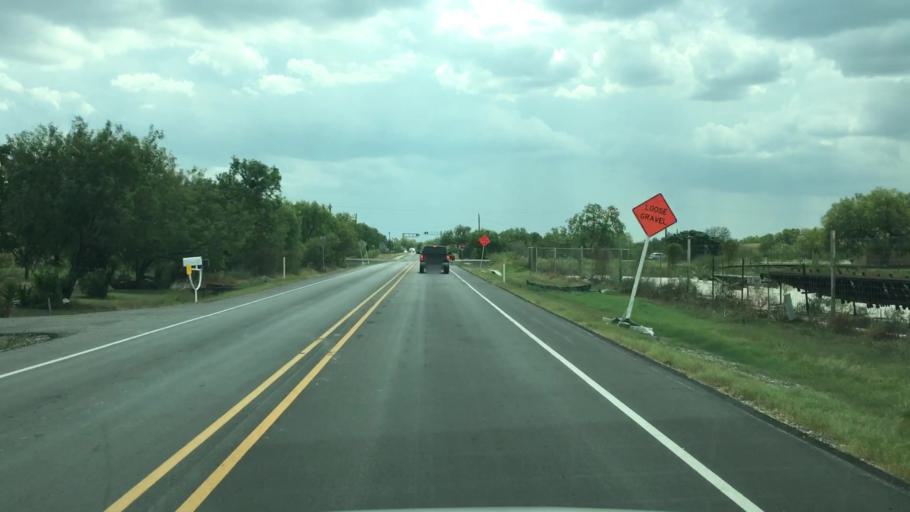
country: US
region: Texas
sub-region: Live Oak County
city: Three Rivers
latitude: 28.6371
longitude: -98.2739
